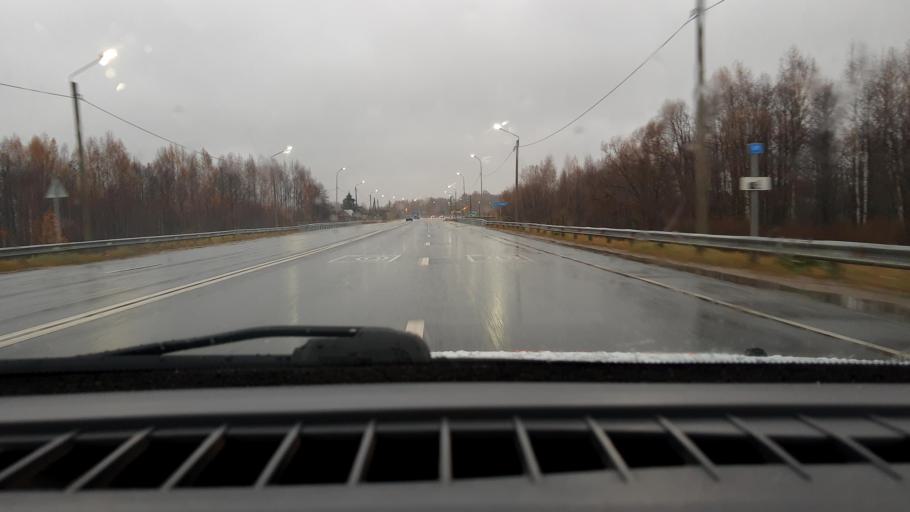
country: RU
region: Nizjnij Novgorod
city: Sitniki
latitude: 56.5038
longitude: 44.0244
